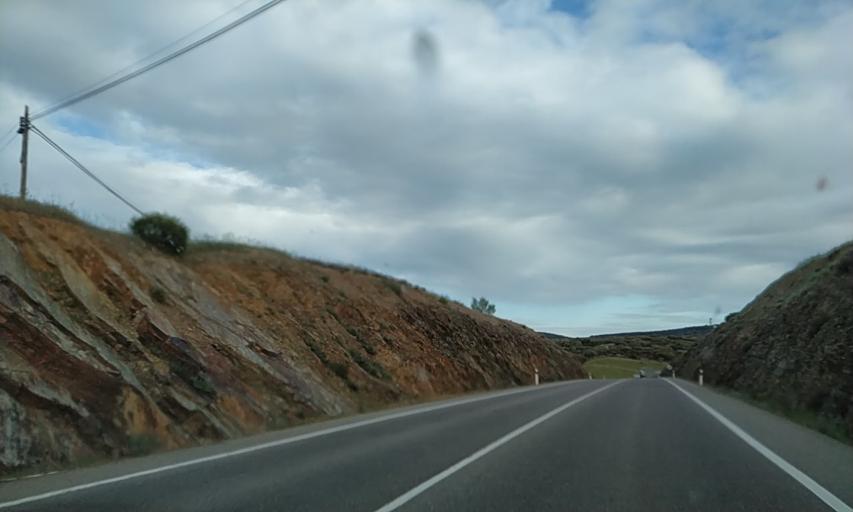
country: ES
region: Extremadura
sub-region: Provincia de Caceres
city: Pedroso de Acim
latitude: 39.8361
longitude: -6.3924
